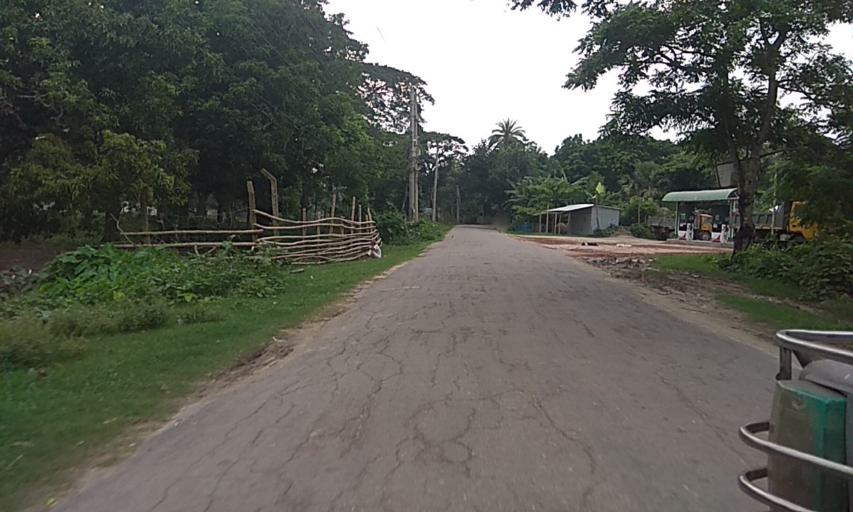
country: BD
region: Dhaka
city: Dohar
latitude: 23.4555
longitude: 90.0157
